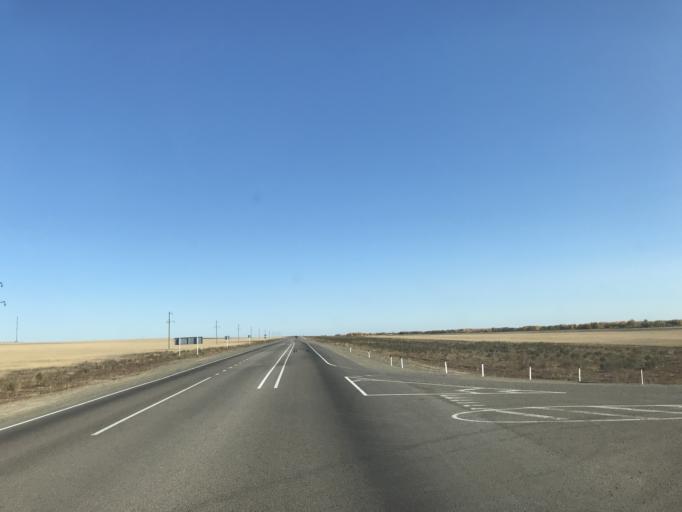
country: KZ
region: Pavlodar
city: Koktobe
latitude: 51.4967
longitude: 77.7175
